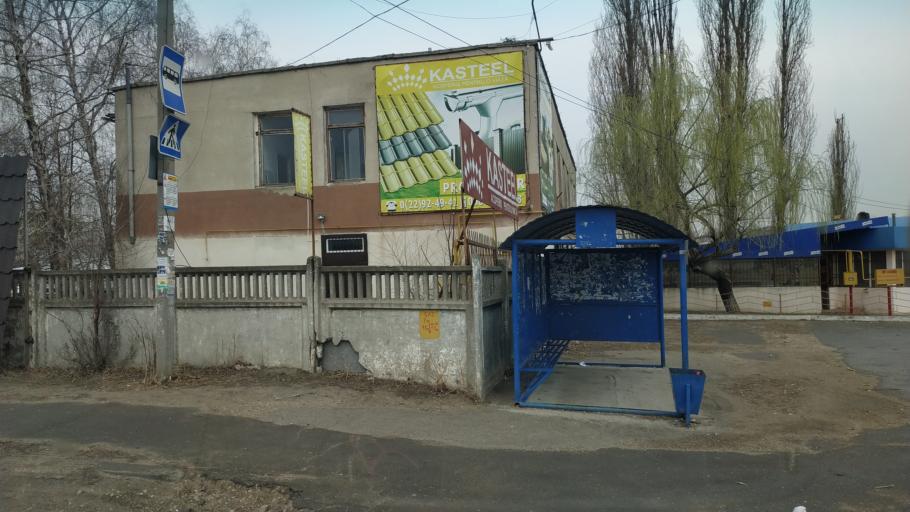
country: MD
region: Chisinau
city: Singera
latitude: 46.9125
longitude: 28.9717
